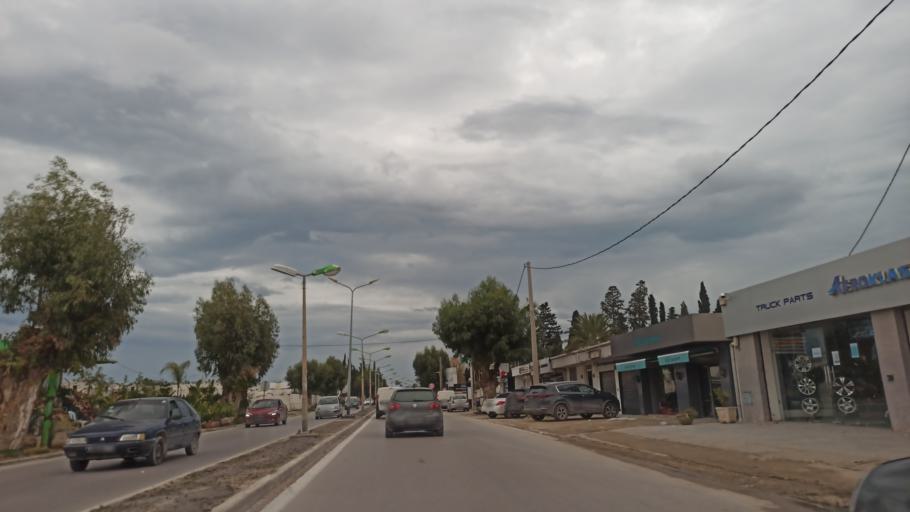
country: TN
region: Ariana
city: Ariana
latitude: 36.8716
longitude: 10.2331
